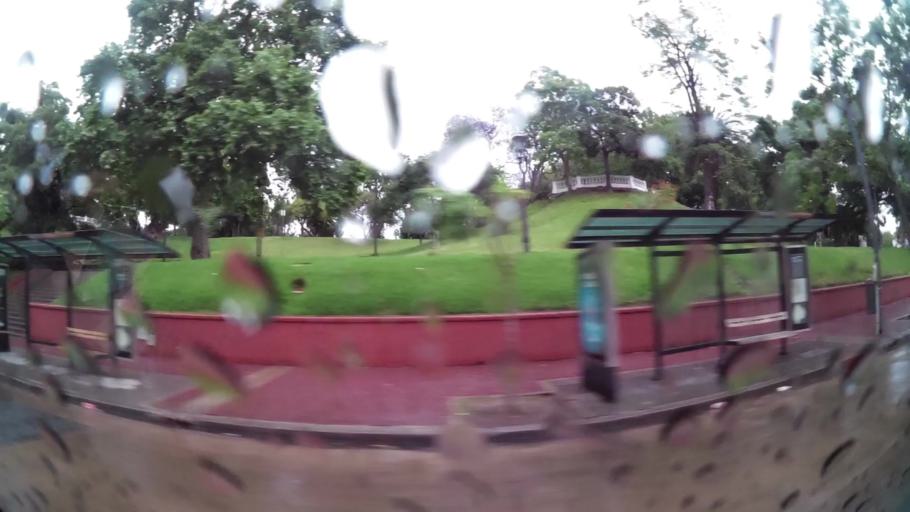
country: AR
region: Buenos Aires F.D.
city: Buenos Aires
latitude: -34.6261
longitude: -58.3681
